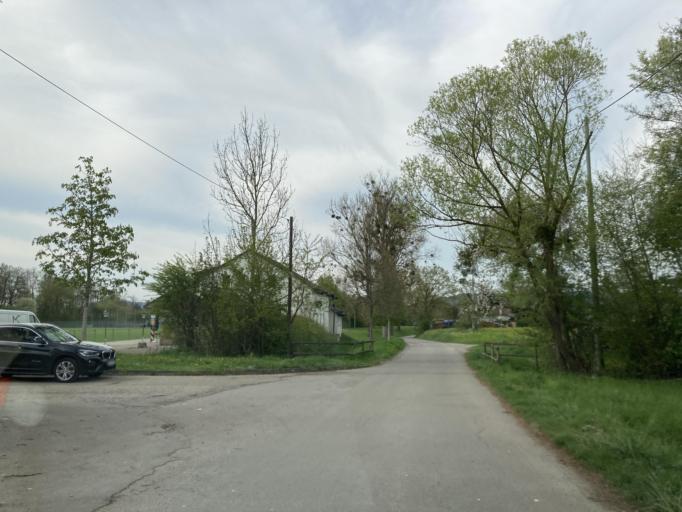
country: DE
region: Baden-Wuerttemberg
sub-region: Tuebingen Region
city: Dusslingen
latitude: 48.4774
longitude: 9.0006
